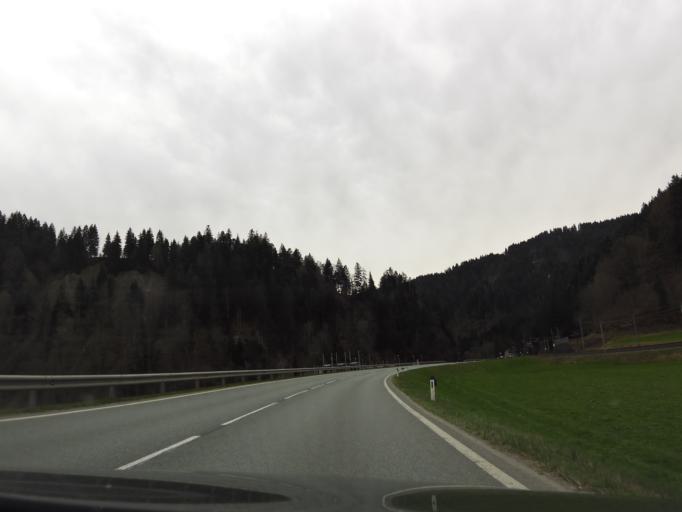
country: AT
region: Tyrol
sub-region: Politischer Bezirk Kitzbuhel
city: Itter
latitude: 47.4740
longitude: 12.1355
